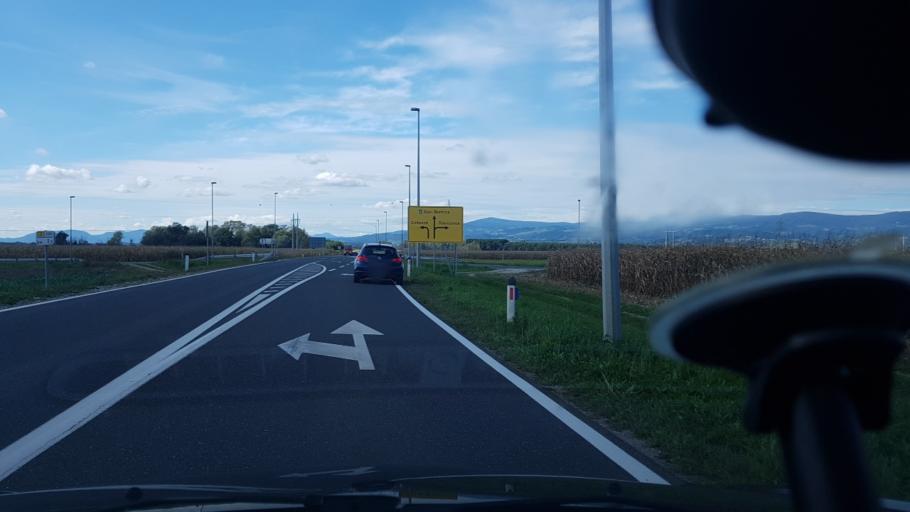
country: SI
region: Majsperk
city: Majsperk
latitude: 46.4090
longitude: 15.7300
